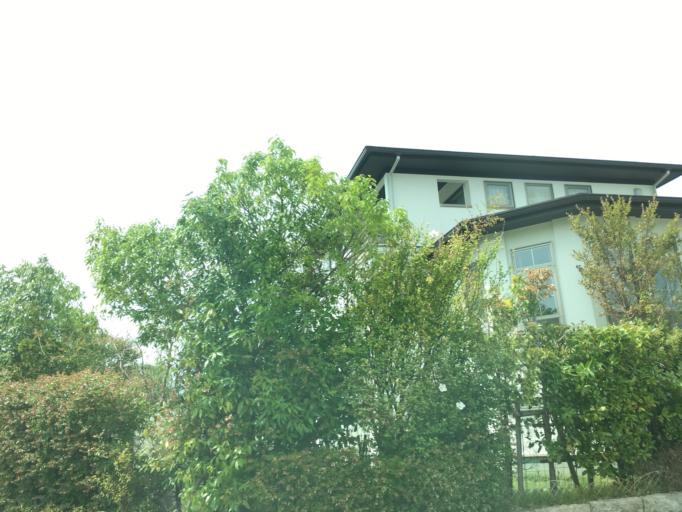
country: JP
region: Hyogo
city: Nishinomiya-hama
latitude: 34.7102
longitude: 135.3148
